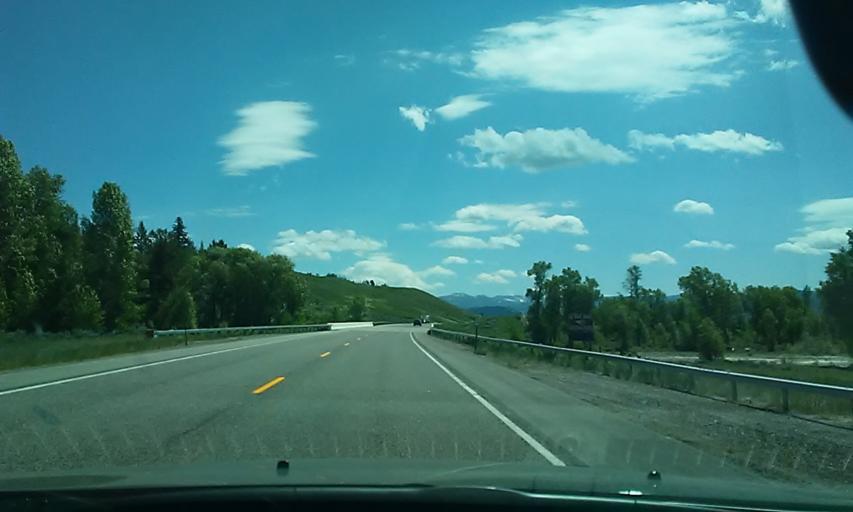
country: US
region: Wyoming
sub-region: Teton County
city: Jackson
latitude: 43.8402
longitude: -110.4590
